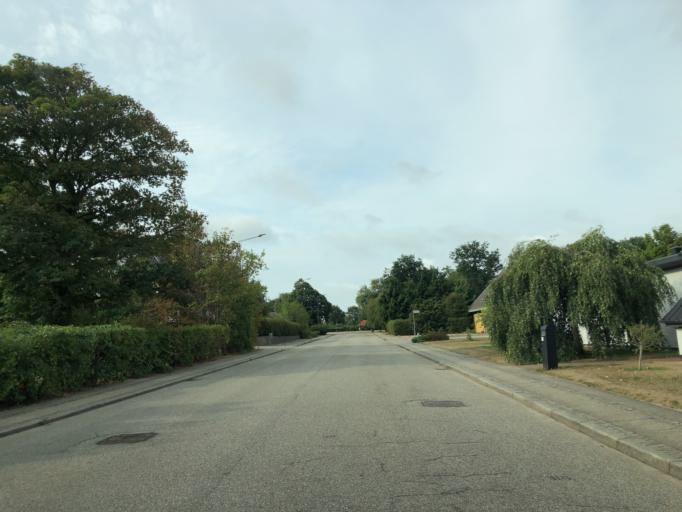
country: DK
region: Central Jutland
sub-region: Ringkobing-Skjern Kommune
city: Tarm
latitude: 55.9059
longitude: 8.5151
